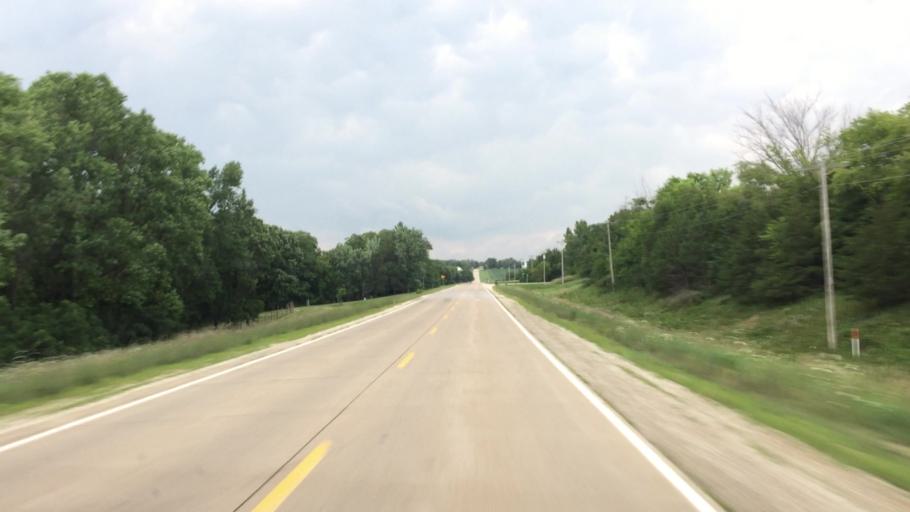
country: US
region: Iowa
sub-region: Lee County
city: Fort Madison
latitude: 40.7160
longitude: -91.3299
